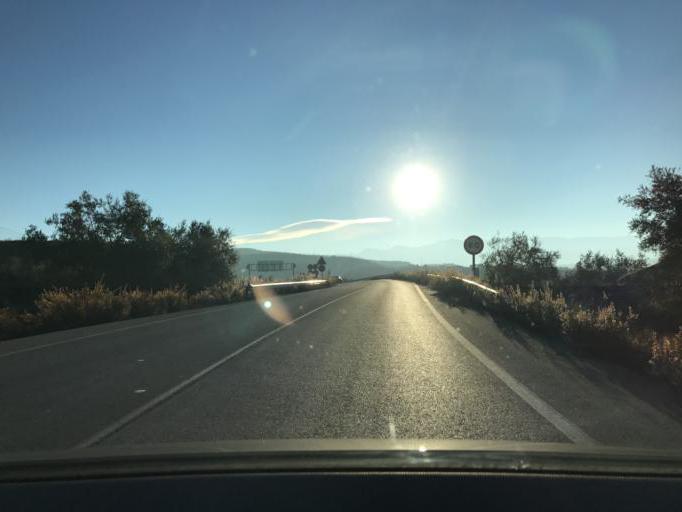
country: ES
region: Andalusia
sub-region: Provincia de Granada
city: Pulianas
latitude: 37.2401
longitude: -3.6092
